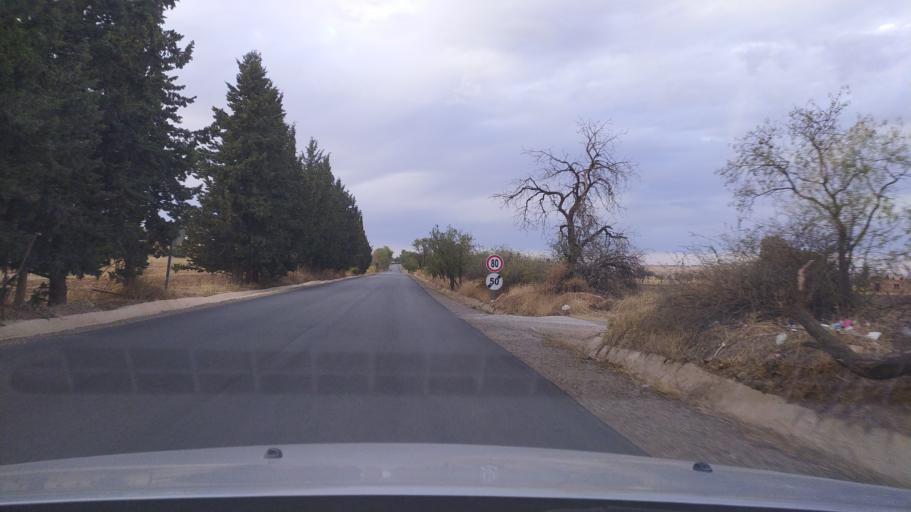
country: DZ
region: Tiaret
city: Frenda
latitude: 35.0322
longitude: 1.0915
